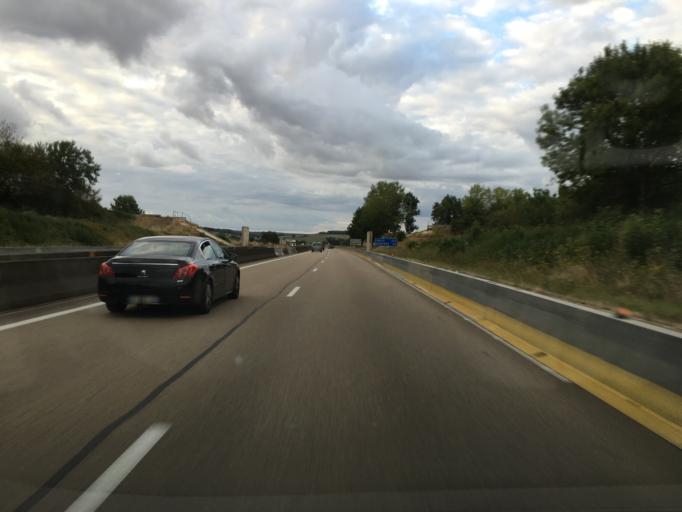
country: FR
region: Bourgogne
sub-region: Departement de l'Yonne
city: Avallon
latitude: 47.5229
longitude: 3.9877
